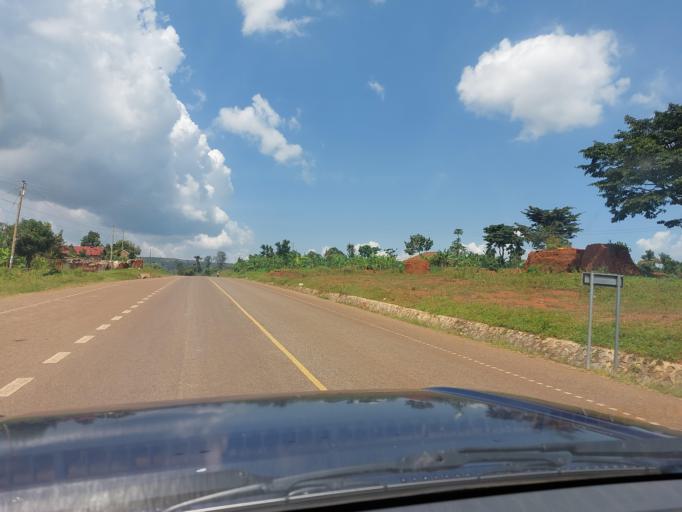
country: UG
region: Central Region
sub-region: Buikwe District
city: Buikwe
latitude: 0.3143
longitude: 33.1070
